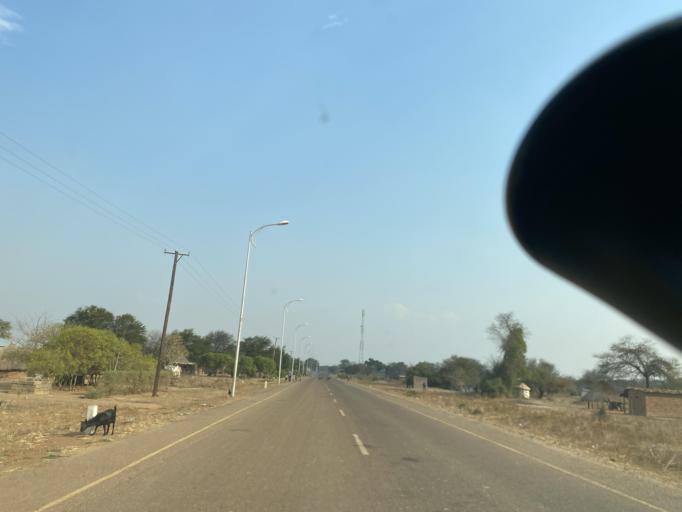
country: ZW
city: Chirundu
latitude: -15.9386
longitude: 28.8730
